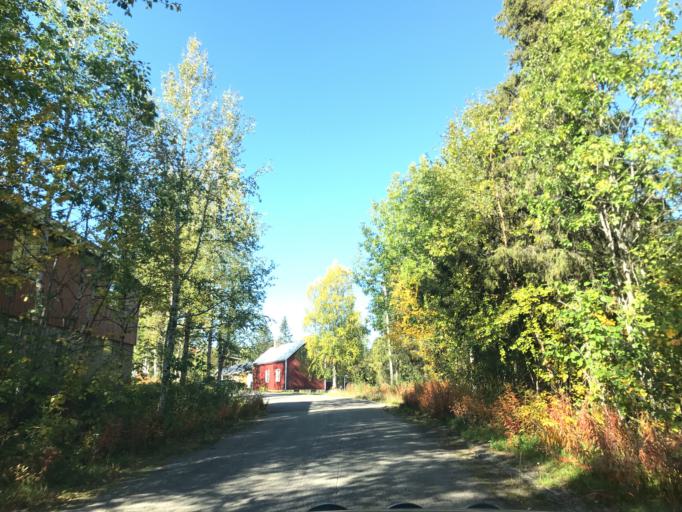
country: SE
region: Norrbotten
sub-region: Gallivare Kommun
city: Malmberget
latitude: 67.6468
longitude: 21.0712
